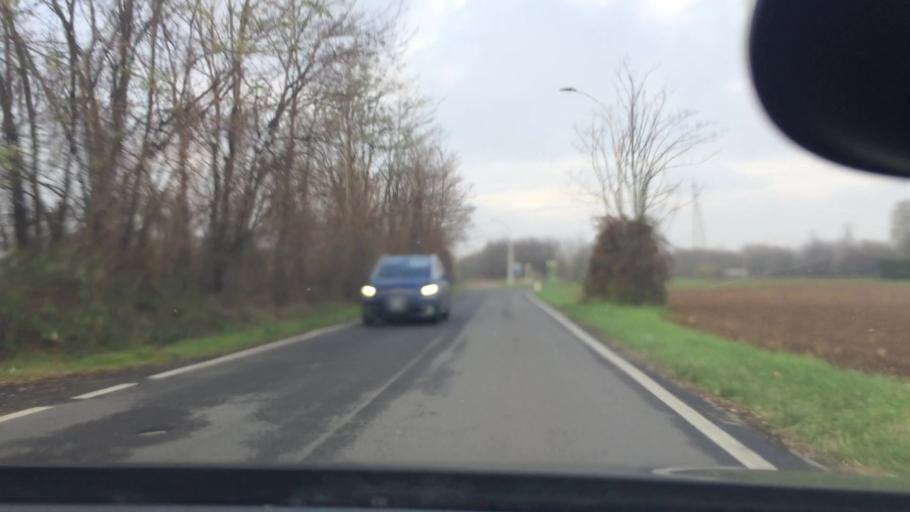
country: IT
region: Lombardy
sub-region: Citta metropolitana di Milano
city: Cerro Maggiore
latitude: 45.6016
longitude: 8.9532
